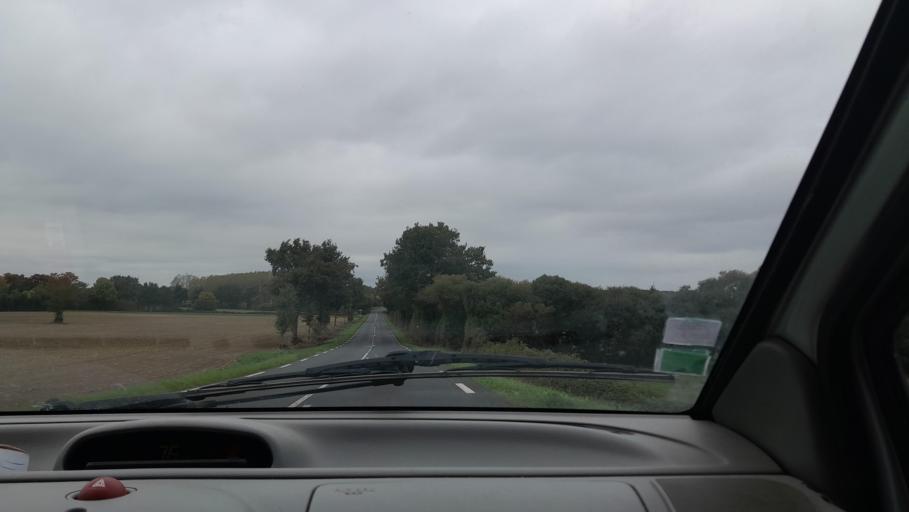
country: FR
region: Pays de la Loire
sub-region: Departement de la Loire-Atlantique
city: Saint-Mars-la-Jaille
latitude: 47.5840
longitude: -1.1926
